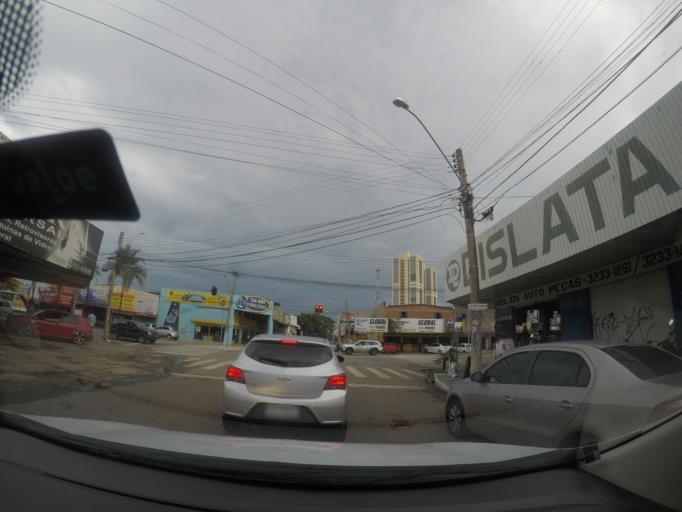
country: BR
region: Goias
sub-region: Goiania
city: Goiania
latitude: -16.6695
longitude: -49.2787
